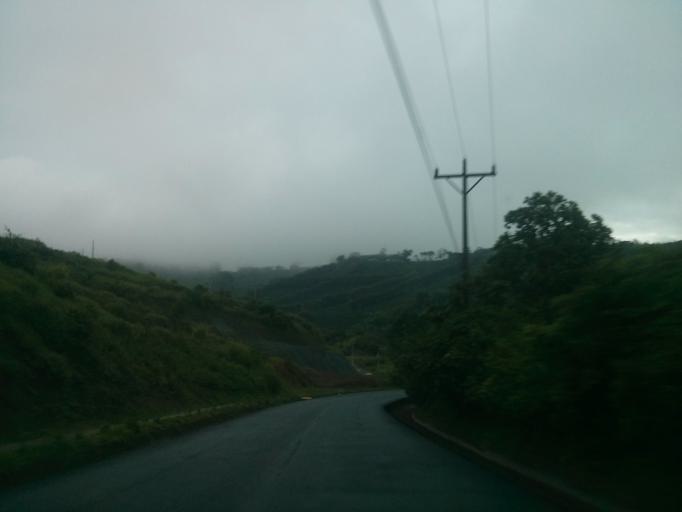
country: CR
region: Alajuela
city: Sabanilla
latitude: 10.0989
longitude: -84.1943
